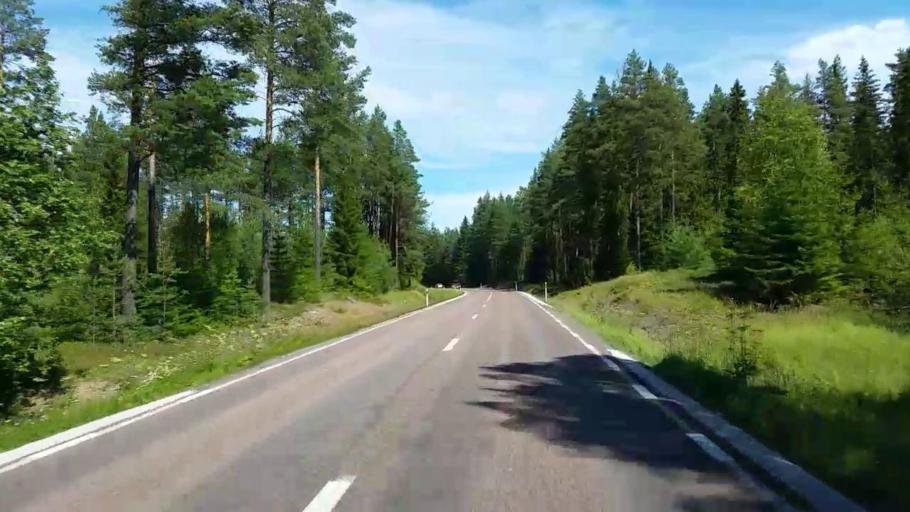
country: SE
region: Dalarna
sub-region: Rattviks Kommun
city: Raettvik
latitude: 60.9097
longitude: 15.1984
